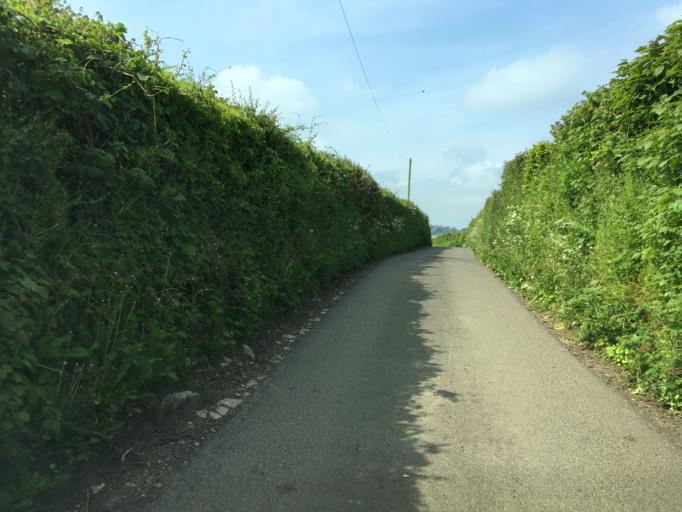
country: GB
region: England
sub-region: North Somerset
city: Winford
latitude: 51.3845
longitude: -2.6581
